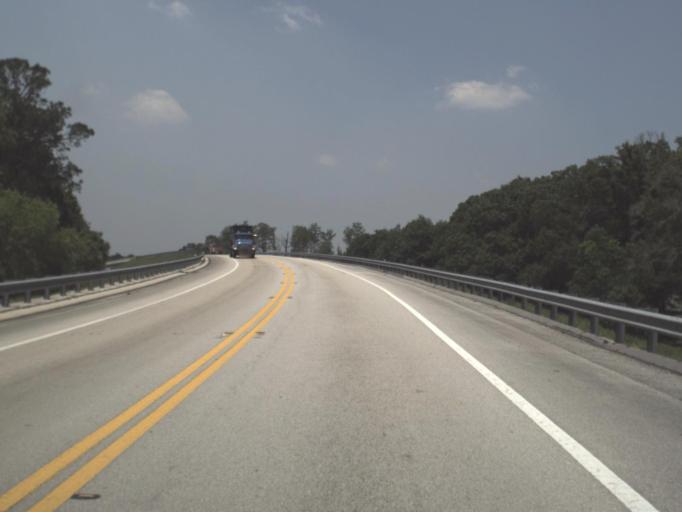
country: US
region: Florida
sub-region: Duval County
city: Baldwin
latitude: 30.2023
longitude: -82.0103
